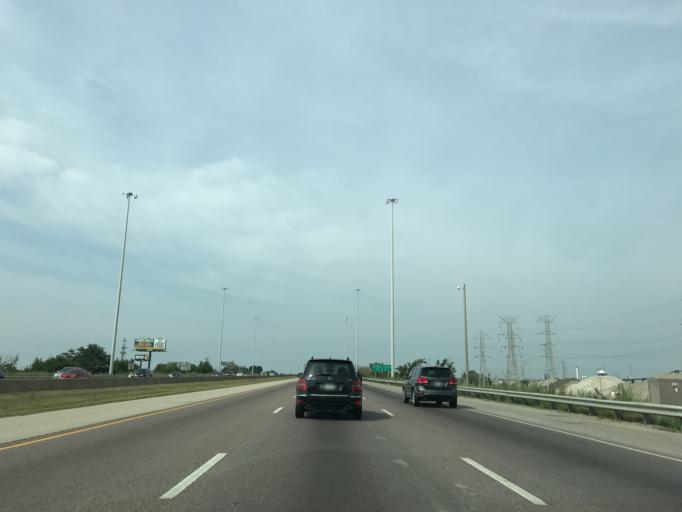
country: US
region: Illinois
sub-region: Cook County
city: Cicero
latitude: 41.8205
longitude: -87.7330
